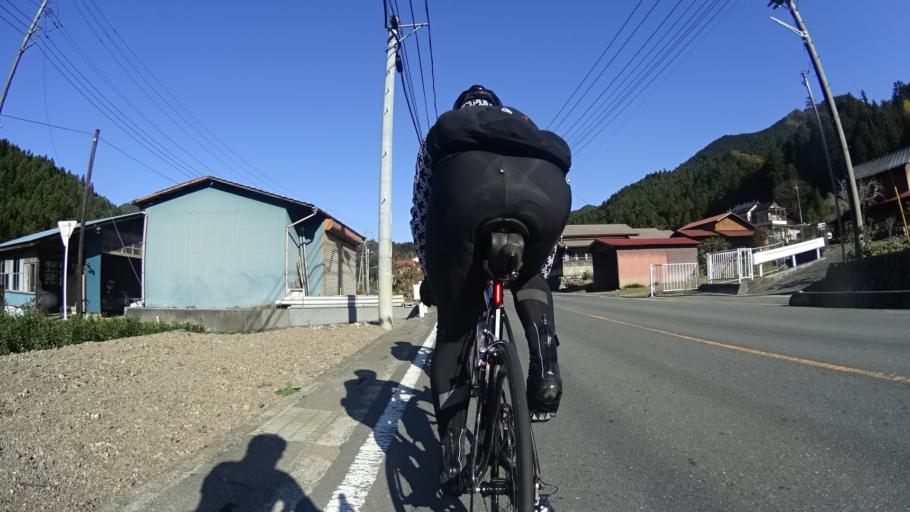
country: JP
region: Tokyo
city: Ome
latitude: 35.8671
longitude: 139.1869
